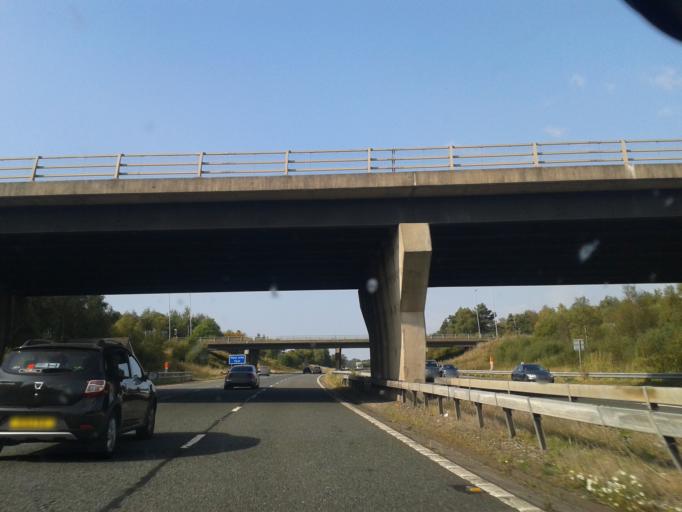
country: GB
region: England
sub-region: Cumbria
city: Carlisle
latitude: 54.9300
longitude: -2.9450
